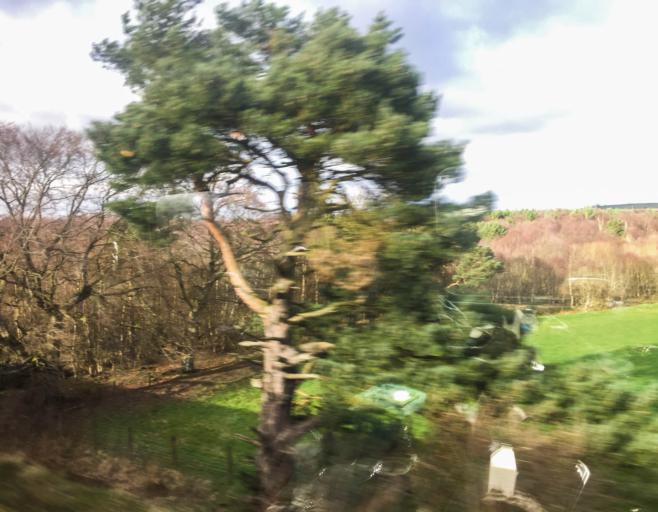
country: GB
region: Scotland
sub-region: South Lanarkshire
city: Carluke
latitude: 55.7058
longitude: -3.8206
